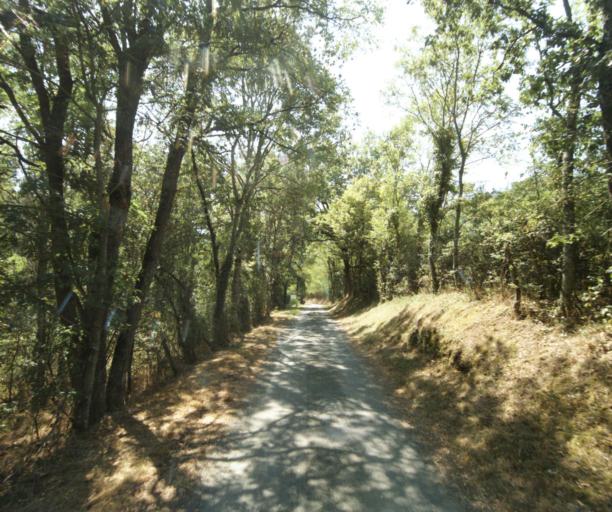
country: FR
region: Rhone-Alpes
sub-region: Departement du Rhone
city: Saint-Pierre-la-Palud
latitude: 45.7884
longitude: 4.6246
